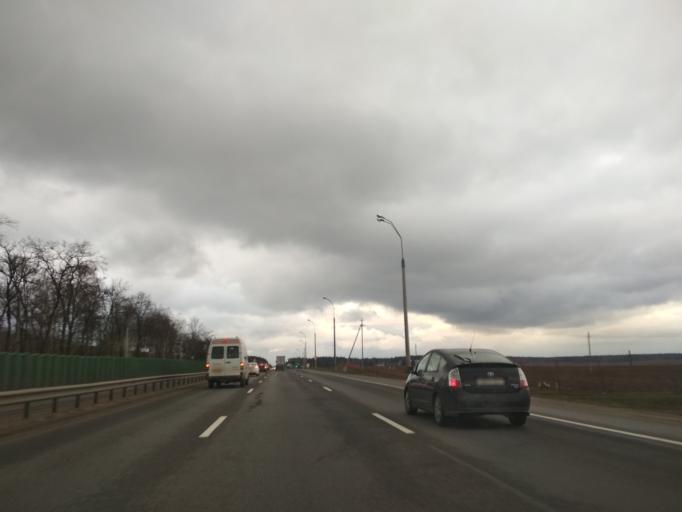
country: BY
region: Minsk
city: Vyaliki Trastsyanets
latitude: 53.8364
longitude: 27.7294
